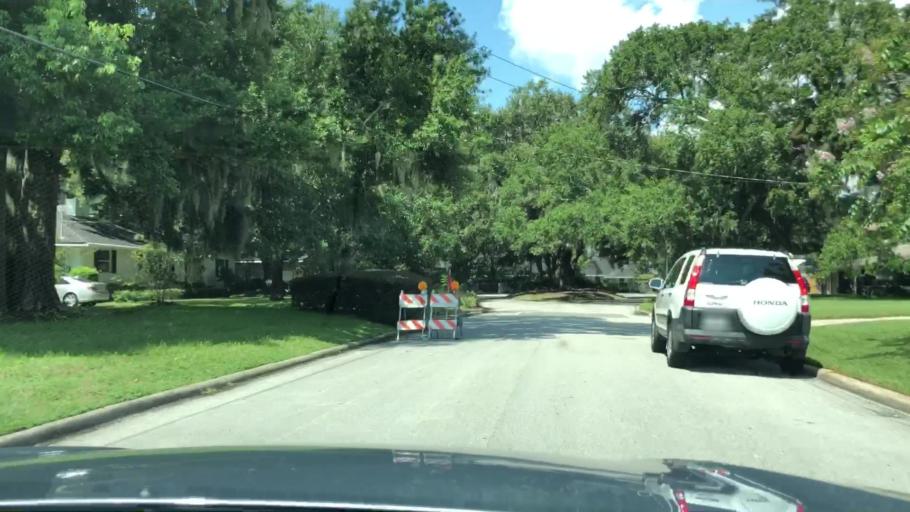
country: US
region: Florida
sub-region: Duval County
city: Jacksonville
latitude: 30.2939
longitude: -81.6526
